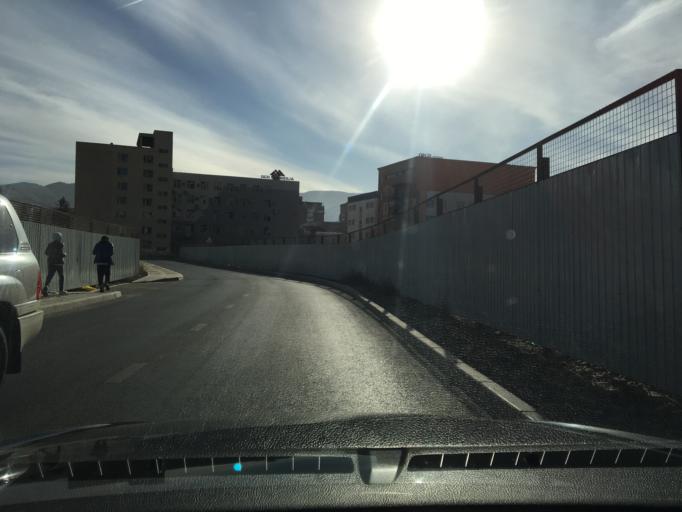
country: MN
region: Ulaanbaatar
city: Ulaanbaatar
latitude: 47.8979
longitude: 106.9146
